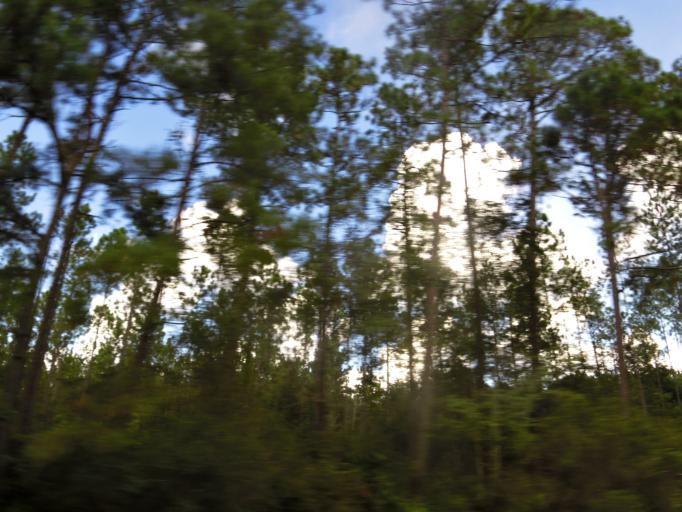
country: US
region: Georgia
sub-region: Echols County
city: Statenville
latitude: 30.7350
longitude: -83.0902
